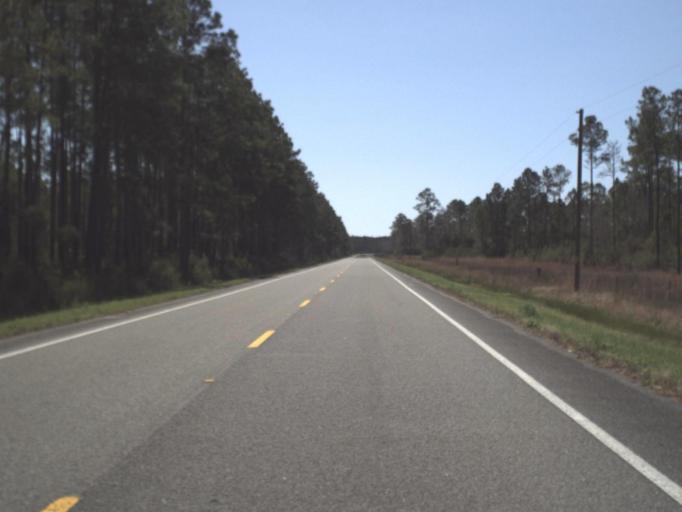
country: US
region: Florida
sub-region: Leon County
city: Woodville
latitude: 30.2393
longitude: -84.0427
